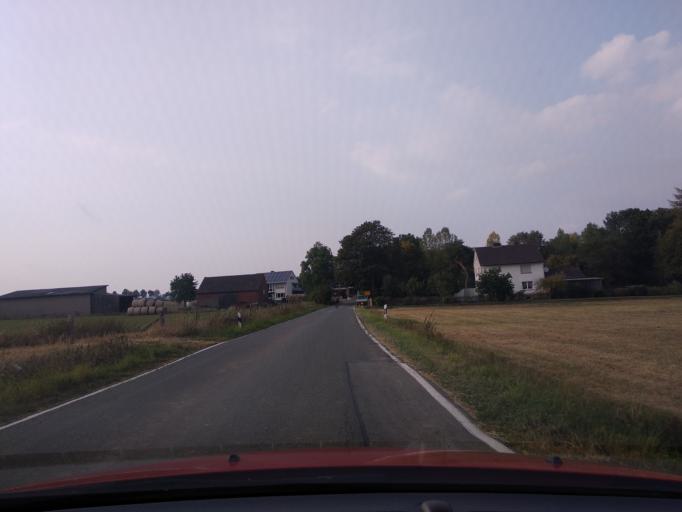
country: DE
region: North Rhine-Westphalia
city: Borgentreich
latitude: 51.5723
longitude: 9.3013
